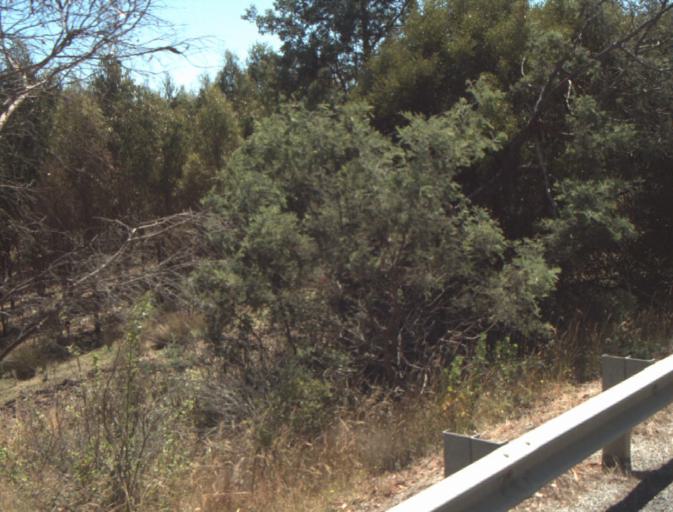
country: AU
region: Tasmania
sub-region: Launceston
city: Newstead
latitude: -41.3860
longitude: 147.3076
